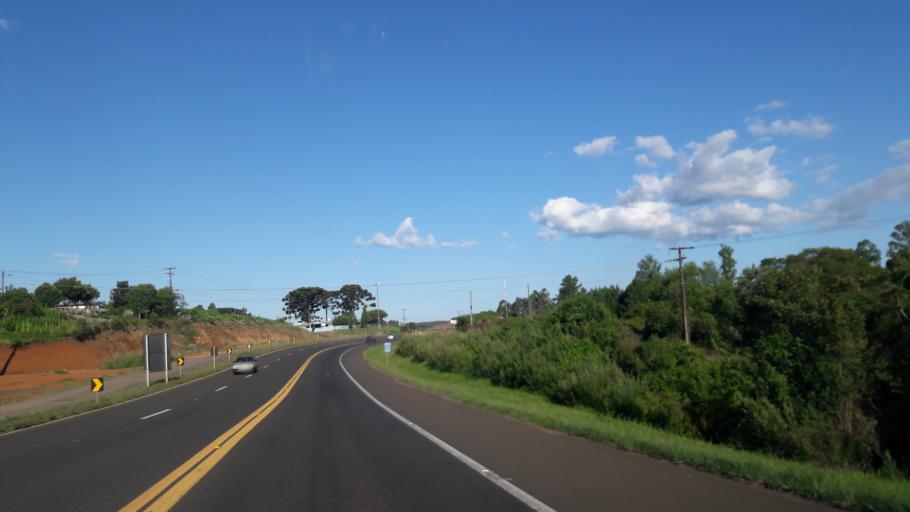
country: BR
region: Parana
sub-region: Guarapuava
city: Guarapuava
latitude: -25.3527
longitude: -51.3685
